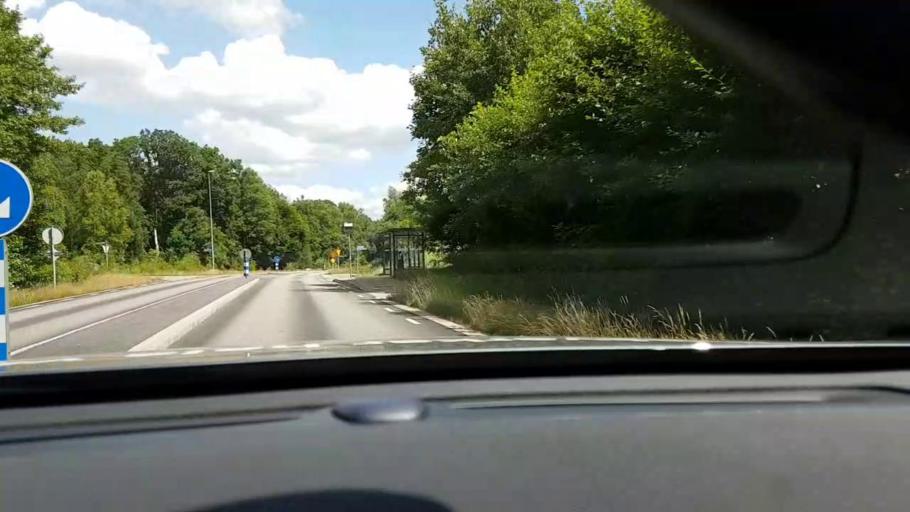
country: SE
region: Skane
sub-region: Hassleholms Kommun
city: Hassleholm
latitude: 56.1674
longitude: 13.7372
